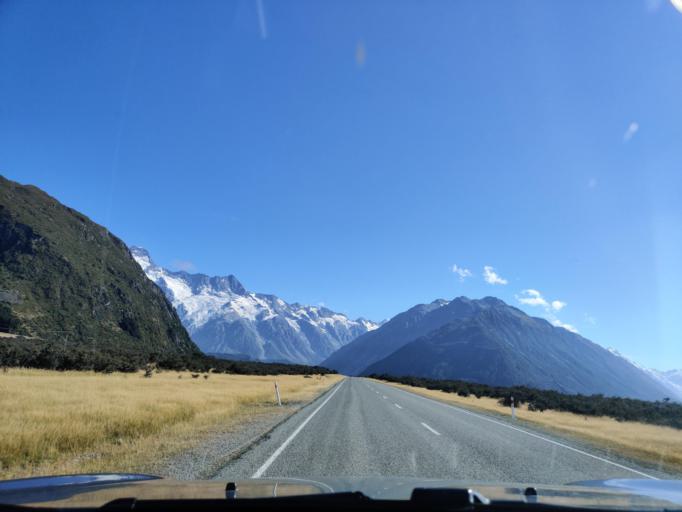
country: NZ
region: Canterbury
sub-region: Timaru District
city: Pleasant Point
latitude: -43.7658
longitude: 170.1230
